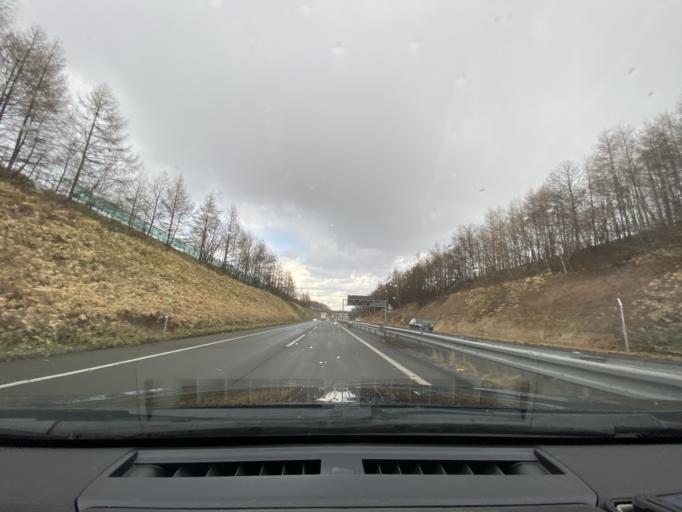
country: JP
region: Hokkaido
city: Otofuke
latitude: 42.9758
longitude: 142.9182
